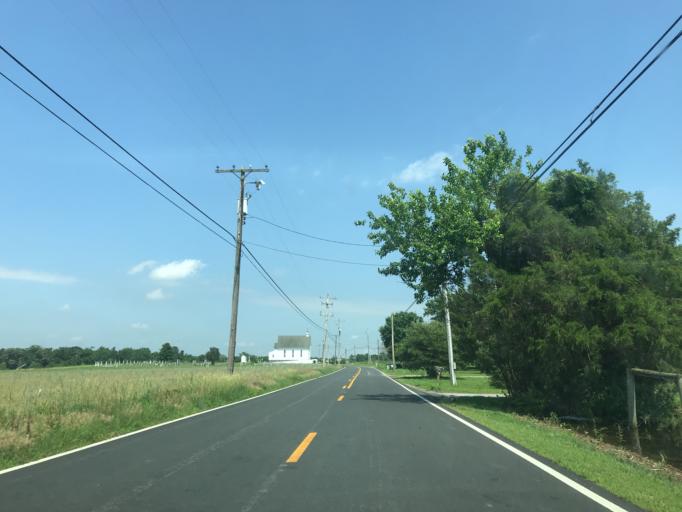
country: US
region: Maryland
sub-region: Dorchester County
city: Hurlock
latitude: 38.5732
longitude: -75.8024
